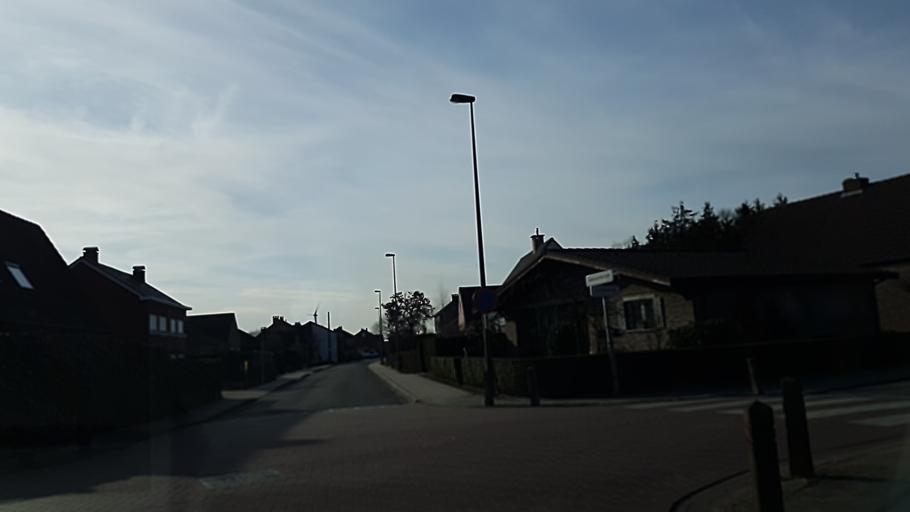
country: BE
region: Flanders
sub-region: Provincie Antwerpen
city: Stabroek
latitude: 51.3565
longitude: 4.3233
